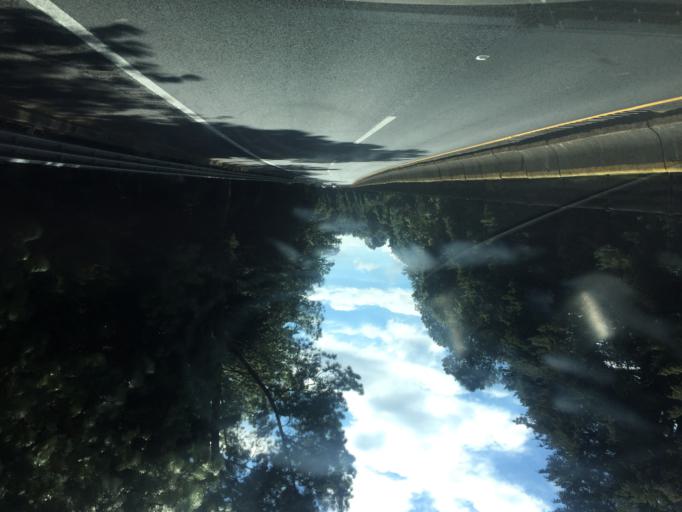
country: MX
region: Morelos
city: Tres Marias
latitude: 19.0404
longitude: -99.2309
